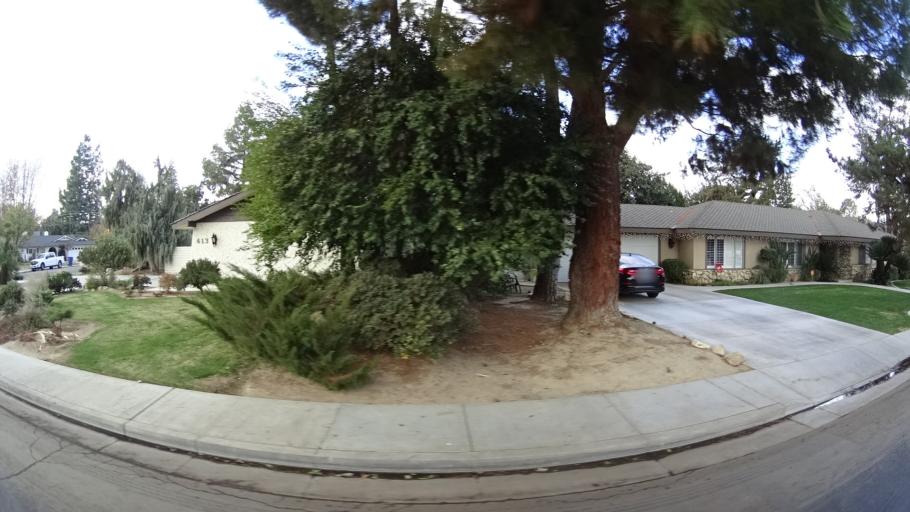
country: US
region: California
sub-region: Kern County
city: Greenacres
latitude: 35.3504
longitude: -119.0831
